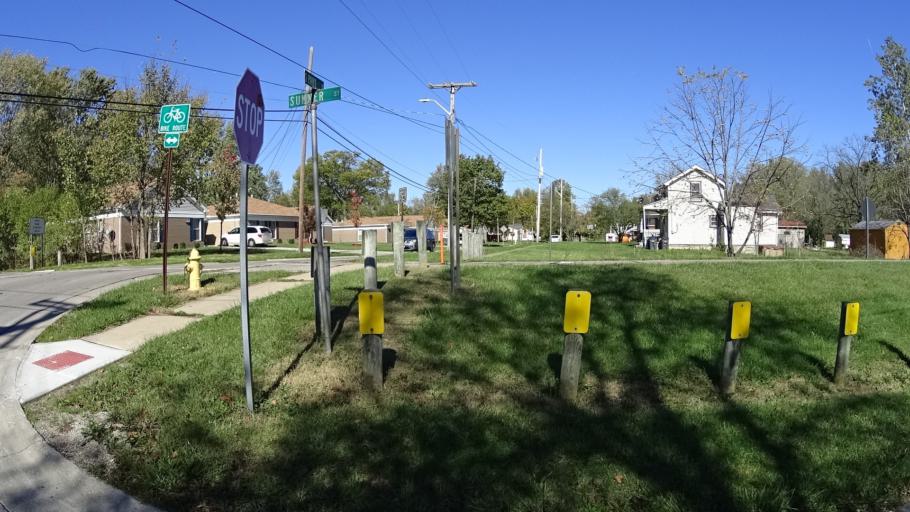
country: US
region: Ohio
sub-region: Lorain County
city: Oberlin
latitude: 41.2850
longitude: -82.2126
